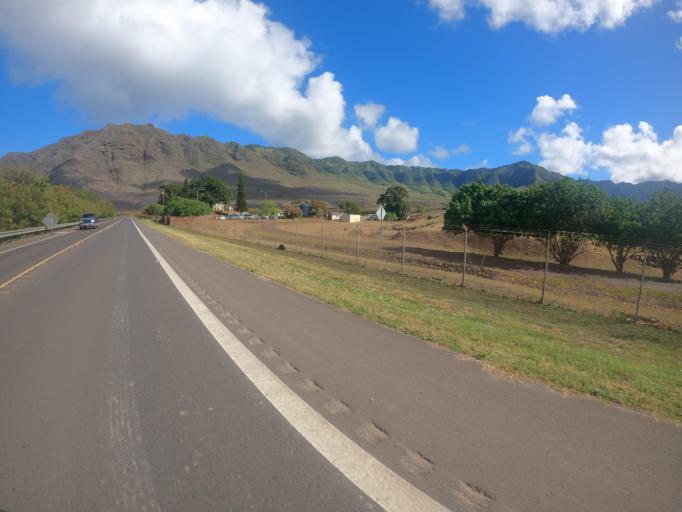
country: US
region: Hawaii
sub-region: Honolulu County
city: Makaha Valley
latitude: 21.5276
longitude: -158.2273
